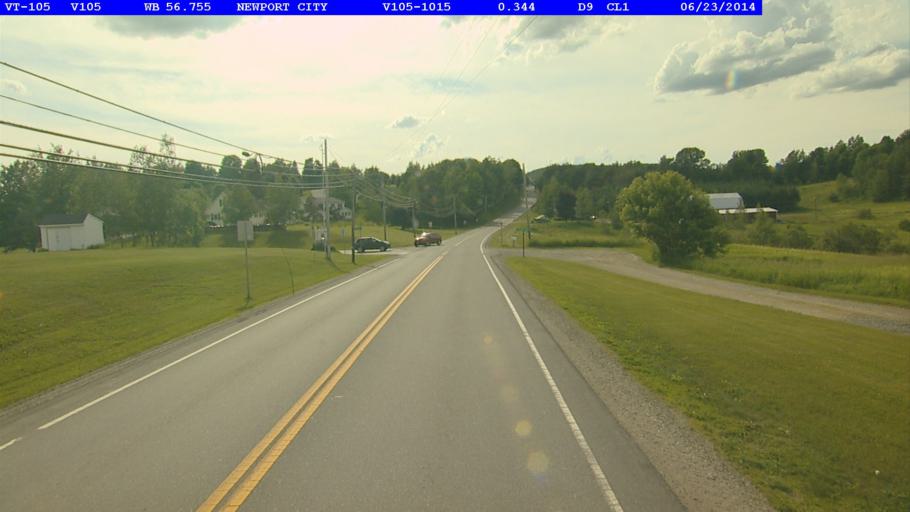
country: US
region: Vermont
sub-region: Orleans County
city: Newport
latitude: 44.9304
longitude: -72.2351
